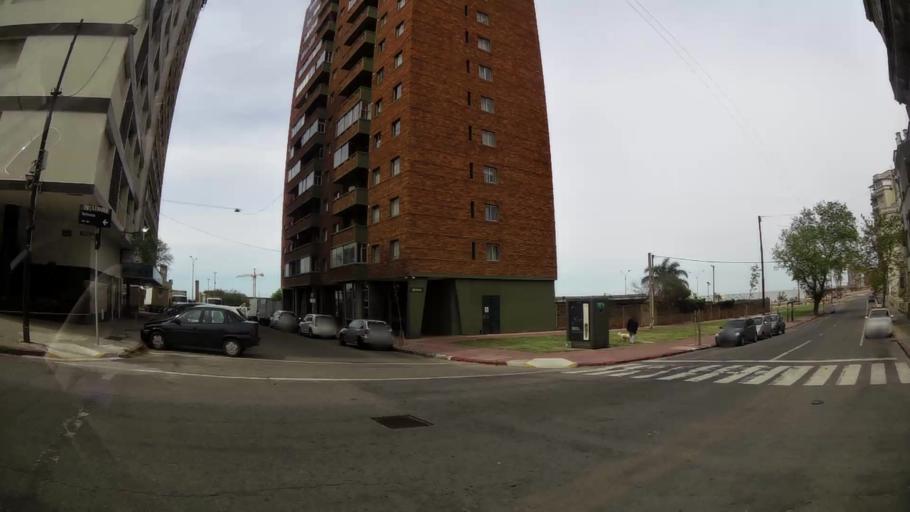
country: UY
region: Montevideo
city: Montevideo
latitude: -34.9102
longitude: -56.1988
